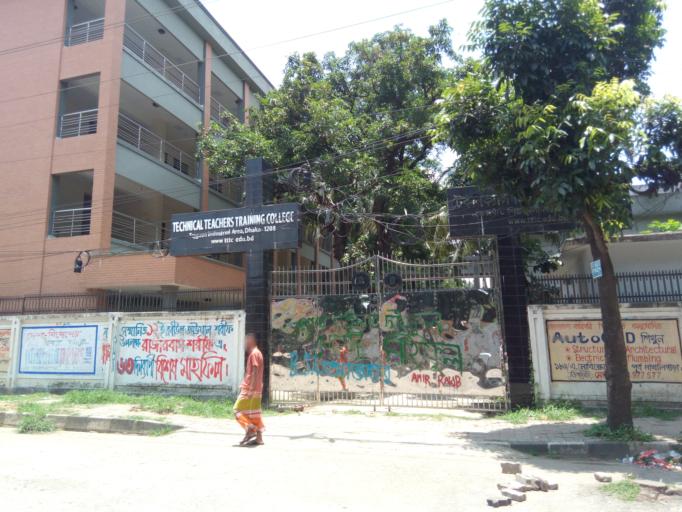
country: BD
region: Dhaka
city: Paltan
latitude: 23.7585
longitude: 90.3998
